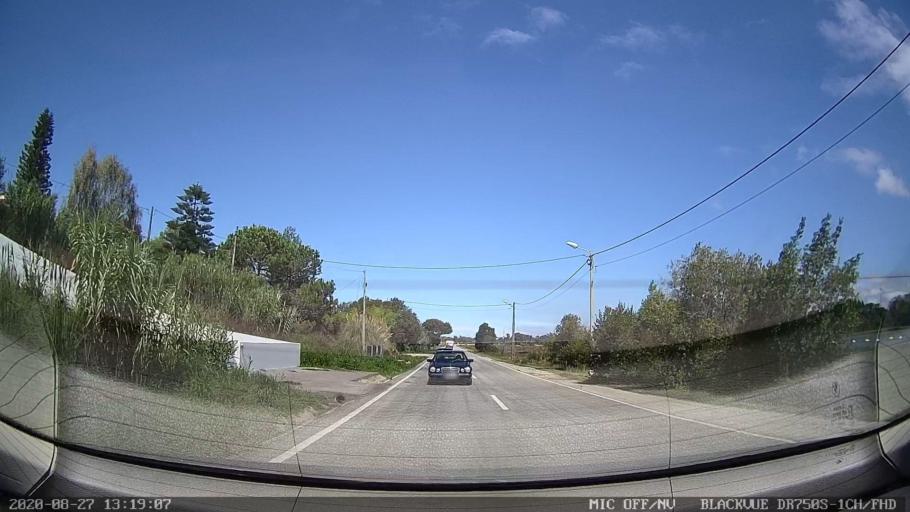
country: PT
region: Aveiro
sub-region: Vagos
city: Vagos
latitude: 40.5674
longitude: -8.6823
